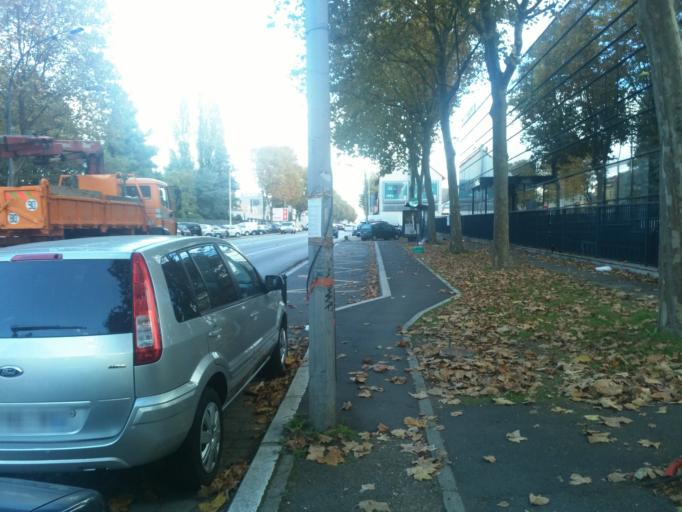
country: FR
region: Ile-de-France
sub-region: Departement de l'Essonne
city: Bievres
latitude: 48.7776
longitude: 2.2325
